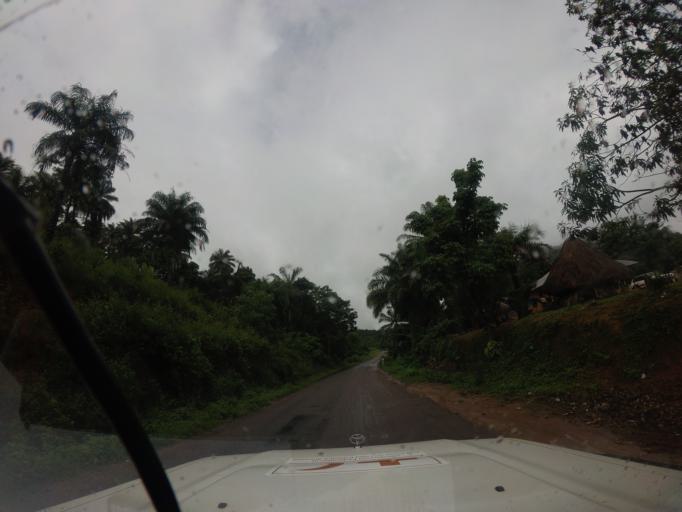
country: SL
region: Northern Province
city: Bumbuna
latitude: 9.3446
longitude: -11.8300
